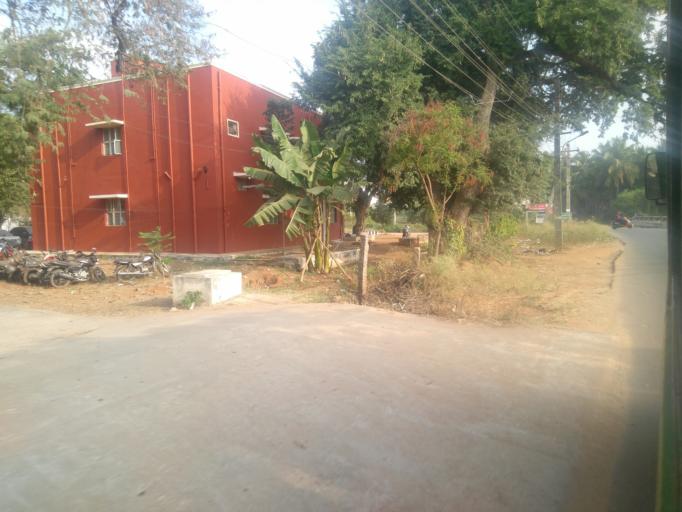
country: IN
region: Tamil Nadu
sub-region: Coimbatore
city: Perur
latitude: 11.0451
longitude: 76.8950
